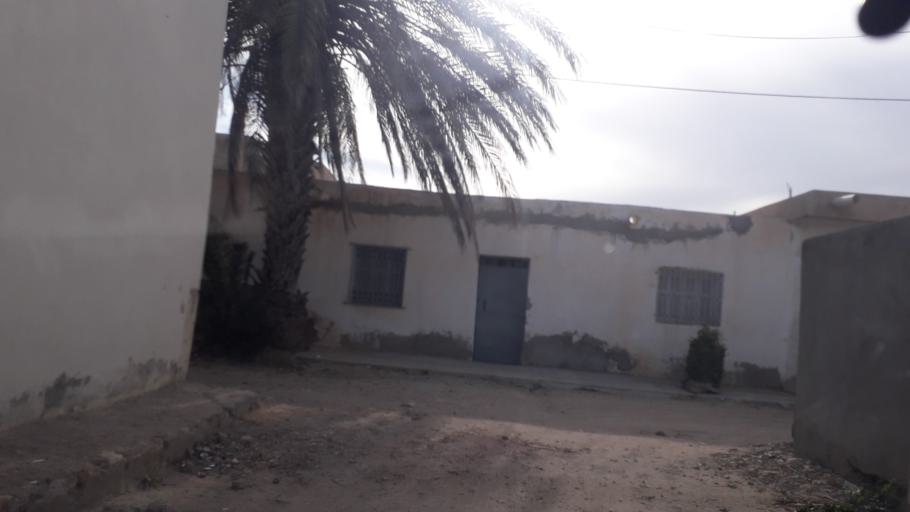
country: TN
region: Safaqis
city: Al Qarmadah
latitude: 34.8854
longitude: 10.7587
